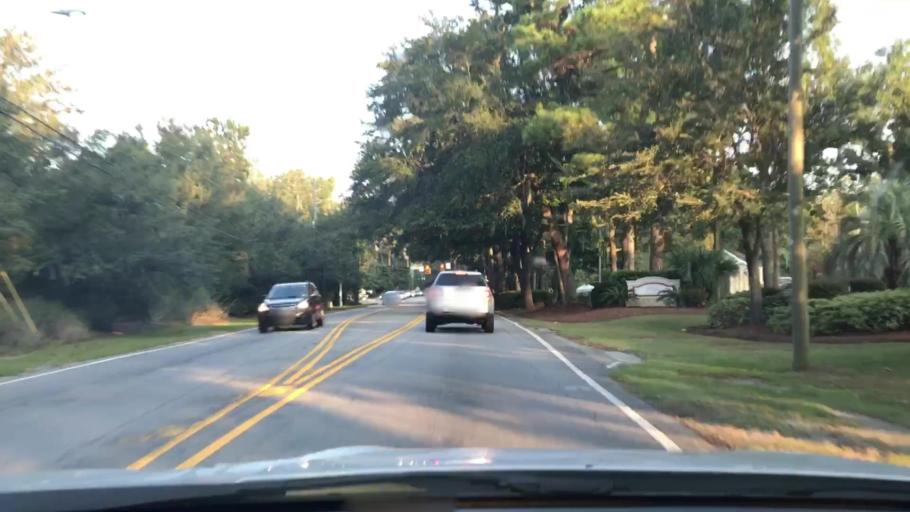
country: US
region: South Carolina
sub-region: Charleston County
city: North Charleston
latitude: 32.8105
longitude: -80.0271
